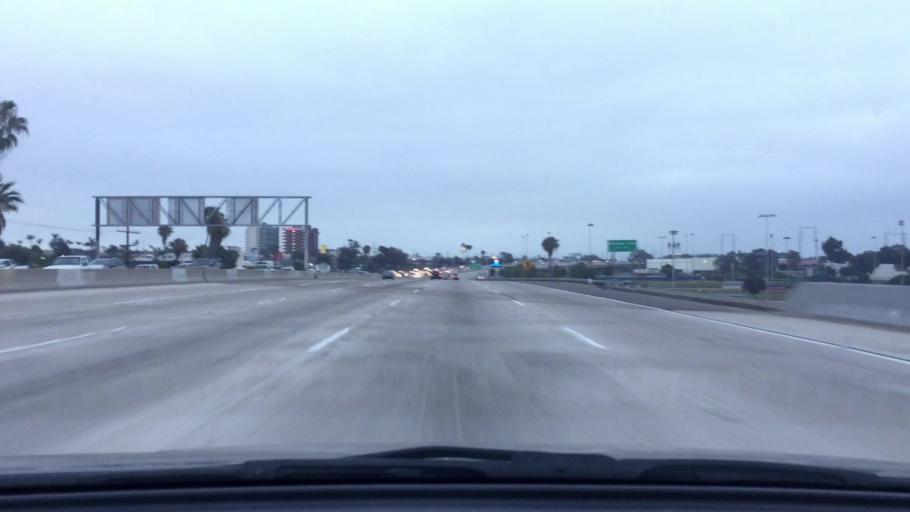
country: US
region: California
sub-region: San Diego County
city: National City
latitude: 32.6826
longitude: -117.1114
